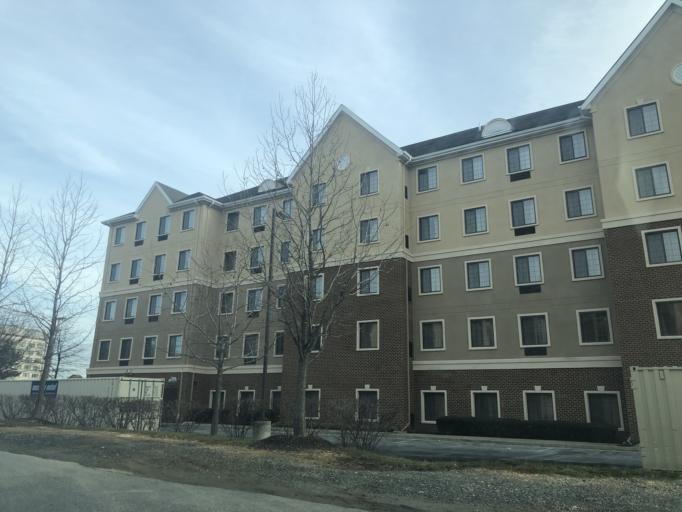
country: US
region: Maryland
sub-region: Howard County
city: Elkridge
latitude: 39.2048
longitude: -76.6927
